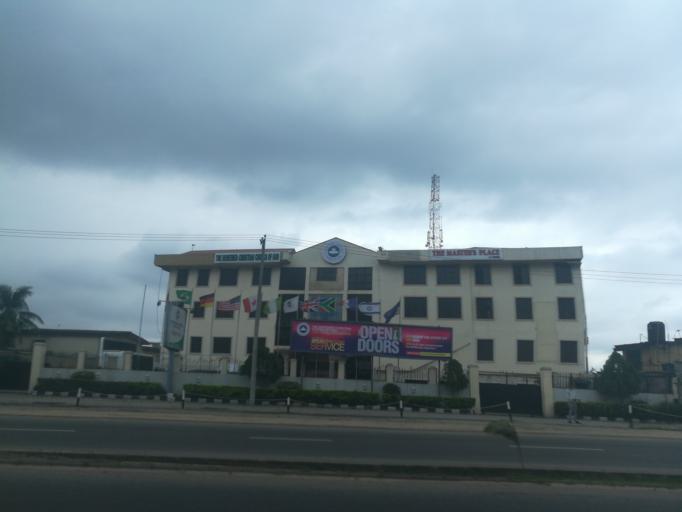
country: NG
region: Lagos
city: Somolu
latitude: 6.5484
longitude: 3.3862
